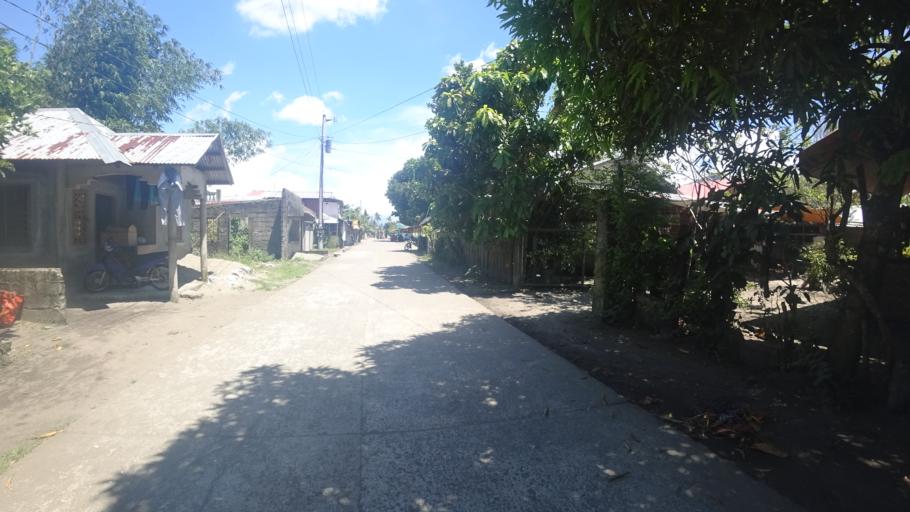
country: PH
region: Eastern Visayas
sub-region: Province of Leyte
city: Mayorga
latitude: 10.8895
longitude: 125.0102
